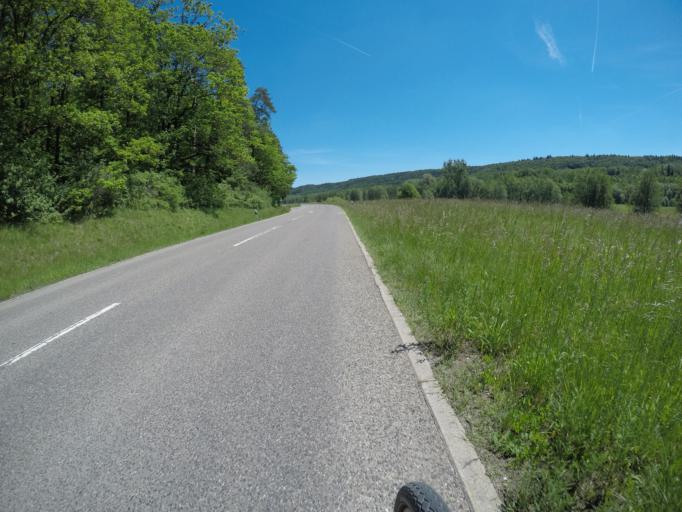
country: DE
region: Baden-Wuerttemberg
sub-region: Regierungsbezirk Stuttgart
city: Magstadt
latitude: 48.7425
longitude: 8.9972
